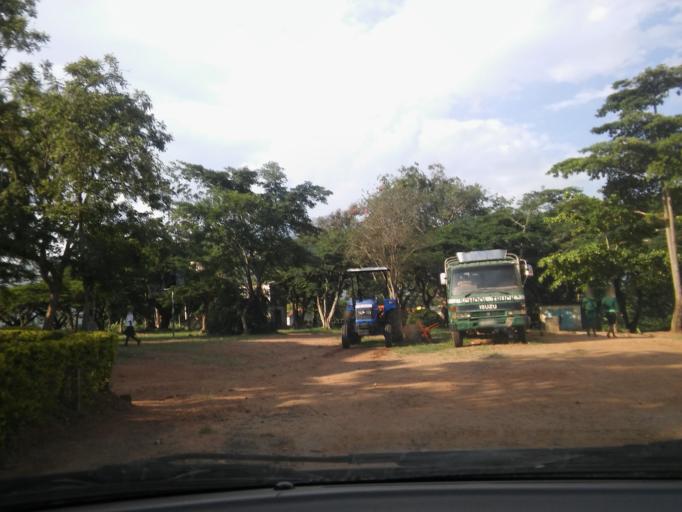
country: UG
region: Eastern Region
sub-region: Mbale District
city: Mbale
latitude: 0.9852
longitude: 34.2108
